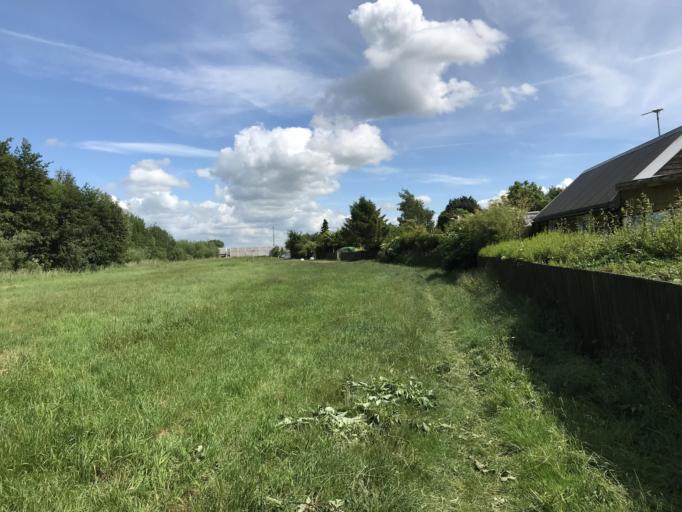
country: SE
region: Skane
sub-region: Landskrona
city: Landskrona
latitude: 55.8955
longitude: 12.8510
